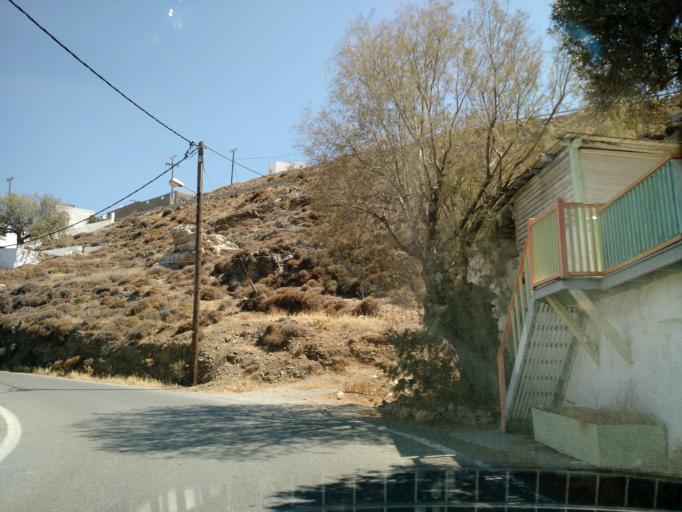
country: GR
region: South Aegean
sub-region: Nomos Dodekanisou
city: Astypalaia
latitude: 36.5480
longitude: 26.3493
